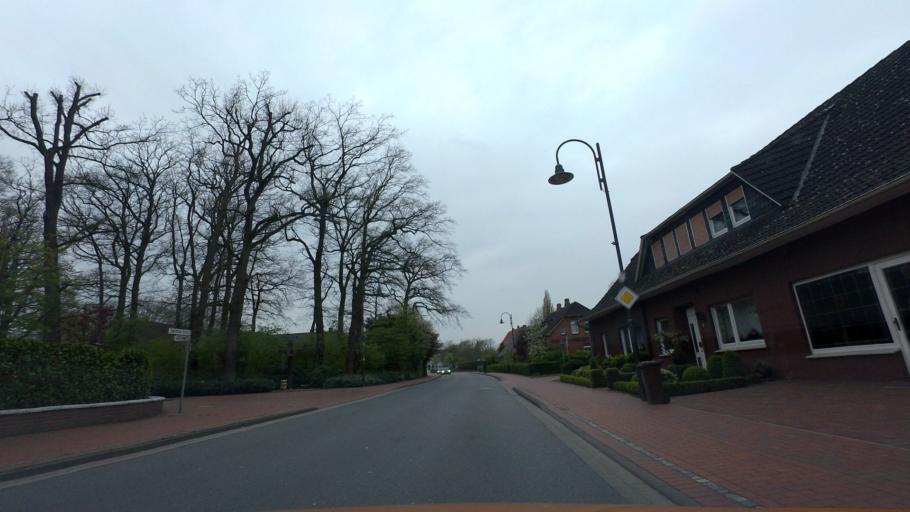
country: DE
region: Lower Saxony
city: Holdorf
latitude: 52.5906
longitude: 8.1253
